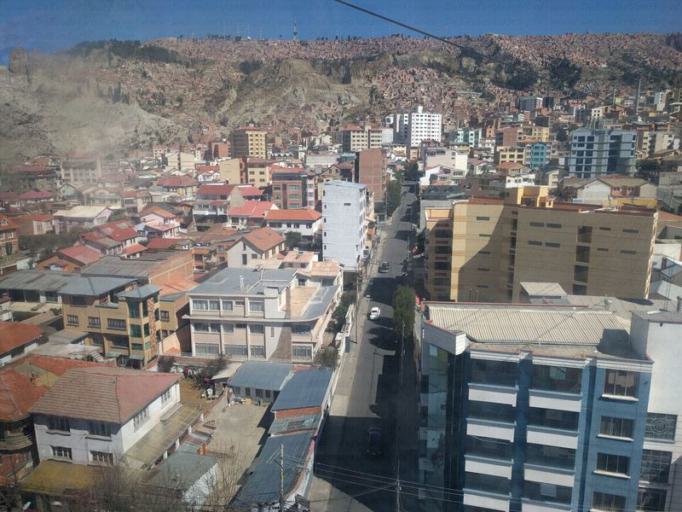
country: BO
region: La Paz
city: La Paz
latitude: -16.5155
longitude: -68.1275
